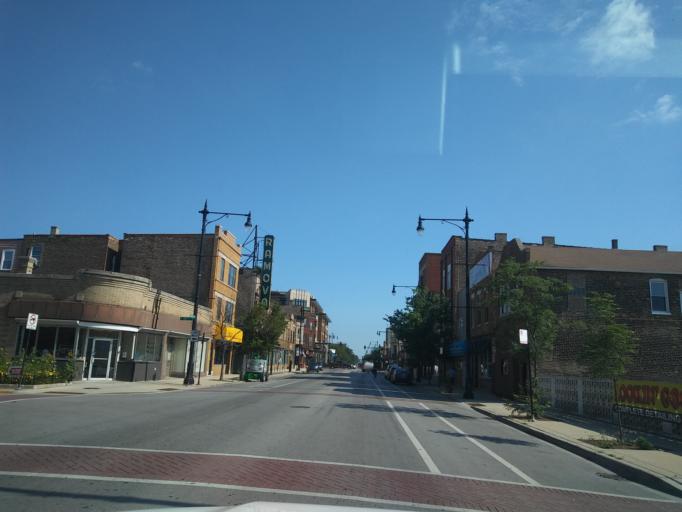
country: US
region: Illinois
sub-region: Cook County
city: Chicago
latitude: 41.8296
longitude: -87.6461
